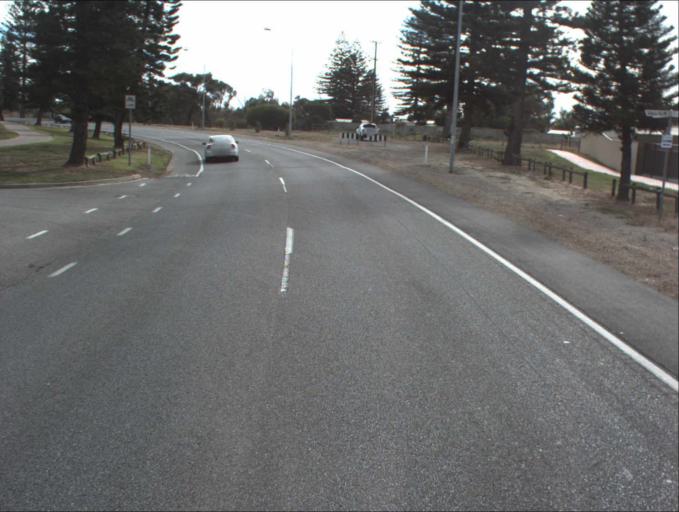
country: AU
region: South Australia
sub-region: Port Adelaide Enfield
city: Birkenhead
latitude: -34.7847
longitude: 138.4898
